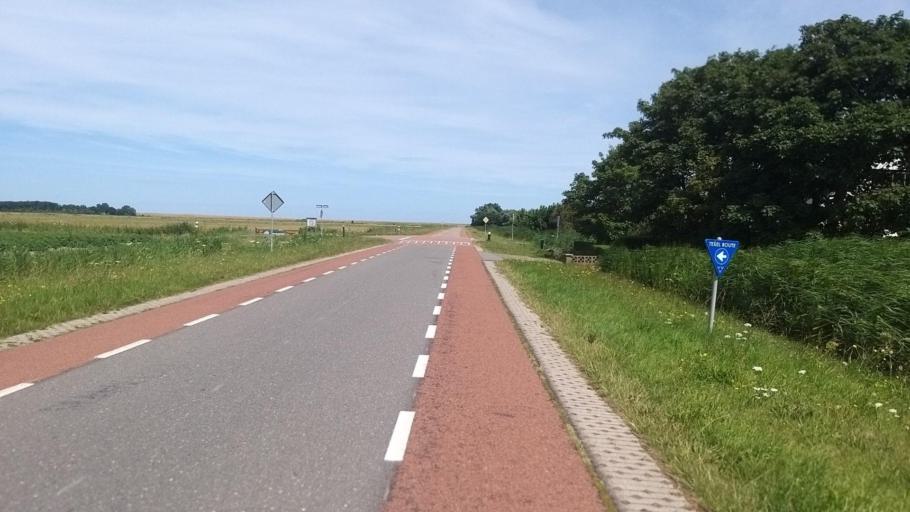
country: NL
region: North Holland
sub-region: Gemeente Texel
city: Den Burg
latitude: 53.1399
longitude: 4.8762
